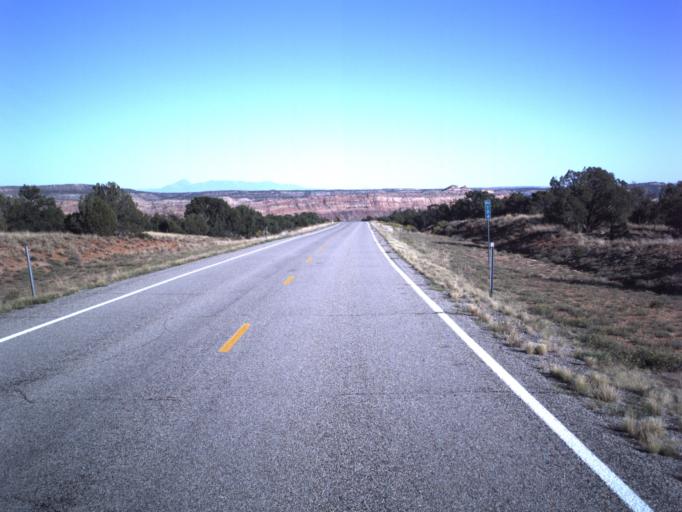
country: US
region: Utah
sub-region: San Juan County
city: Blanding
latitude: 37.5327
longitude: -109.7017
